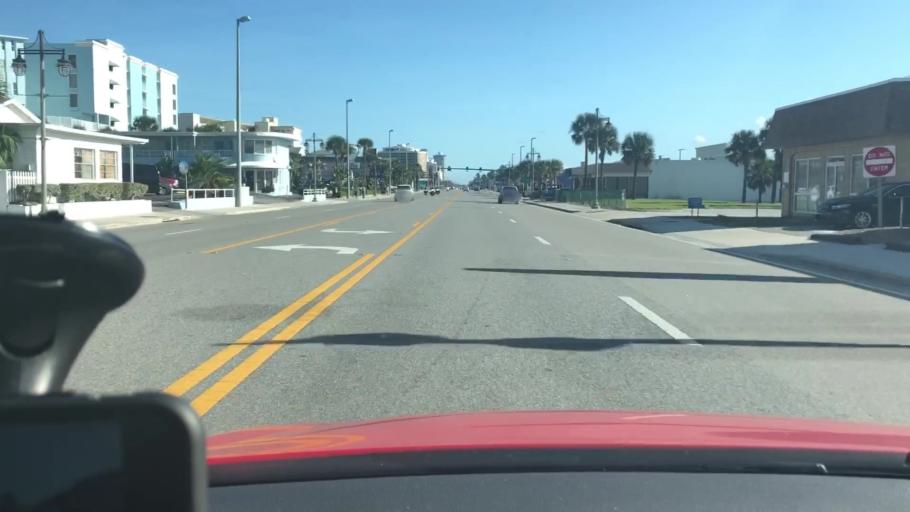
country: US
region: Florida
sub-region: Volusia County
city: Daytona Beach Shores
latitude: 29.1980
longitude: -80.9941
